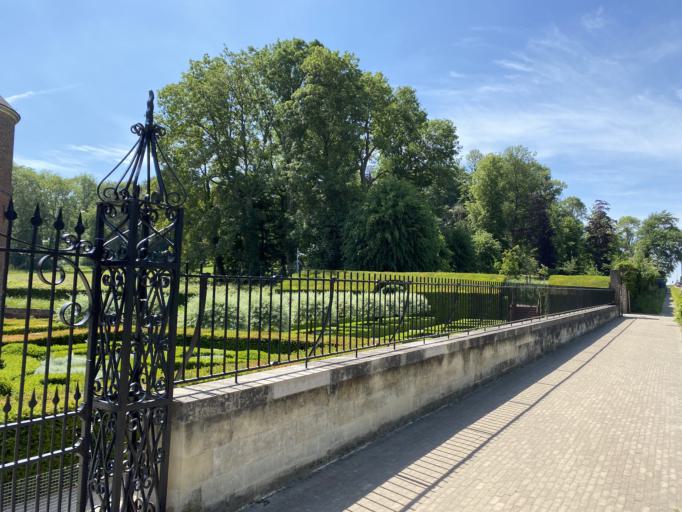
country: BE
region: Flanders
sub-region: Provincie Limburg
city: Bilzen
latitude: 50.8419
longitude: 5.5200
